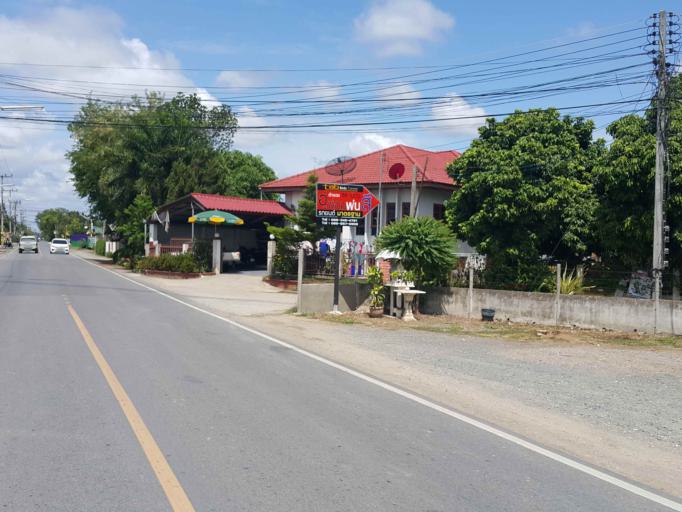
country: TH
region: Chiang Mai
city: Saraphi
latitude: 18.7061
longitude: 99.0254
